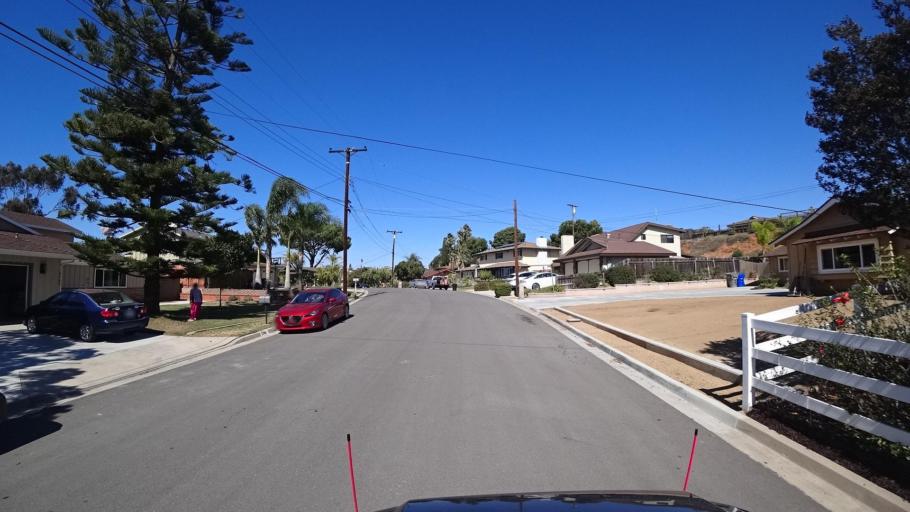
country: US
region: California
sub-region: San Diego County
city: Chula Vista
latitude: 32.6549
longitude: -117.0632
